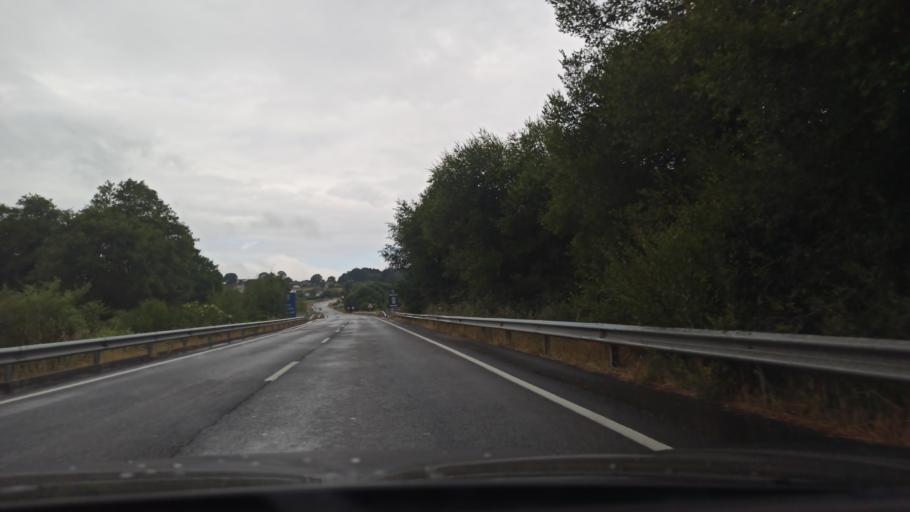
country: ES
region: Galicia
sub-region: Provincia de Lugo
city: Monterroso
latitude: 42.7907
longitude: -7.8554
